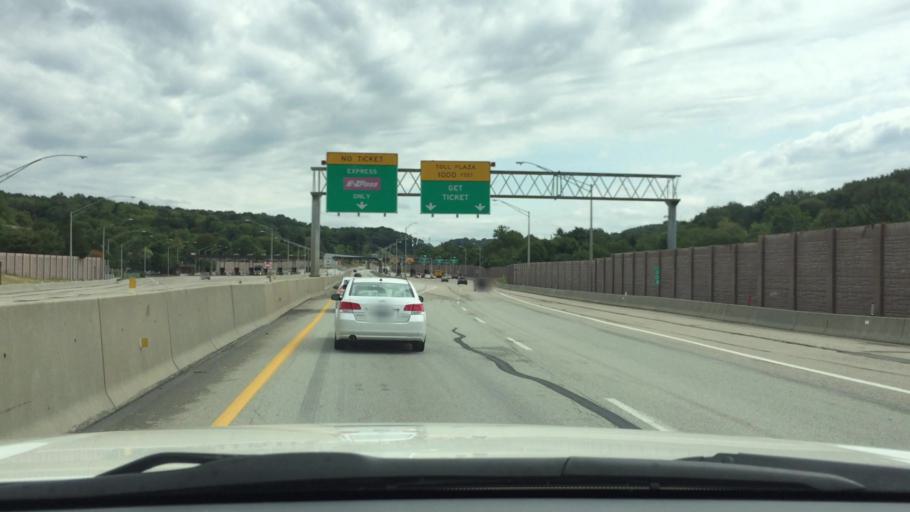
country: US
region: Pennsylvania
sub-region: Allegheny County
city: Bradford Woods
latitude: 40.6559
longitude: -80.0766
